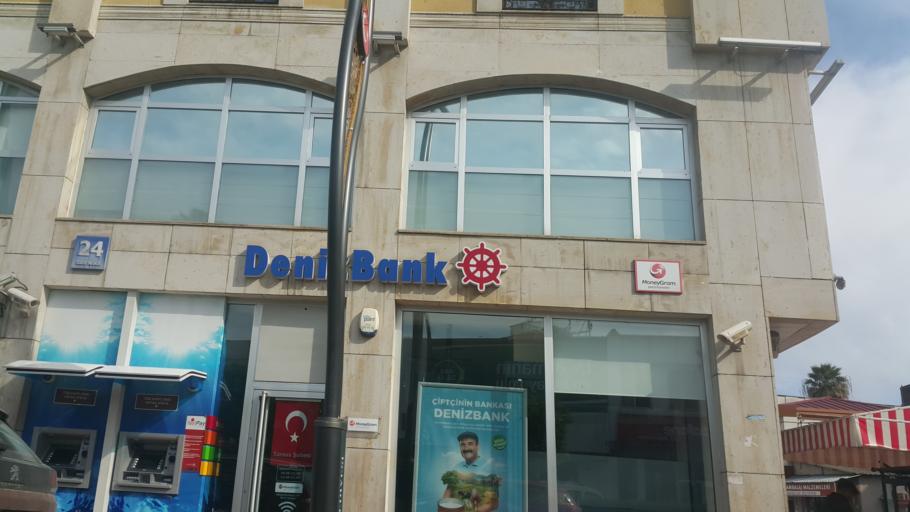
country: TR
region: Mersin
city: Tarsus
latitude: 36.9161
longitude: 34.8947
